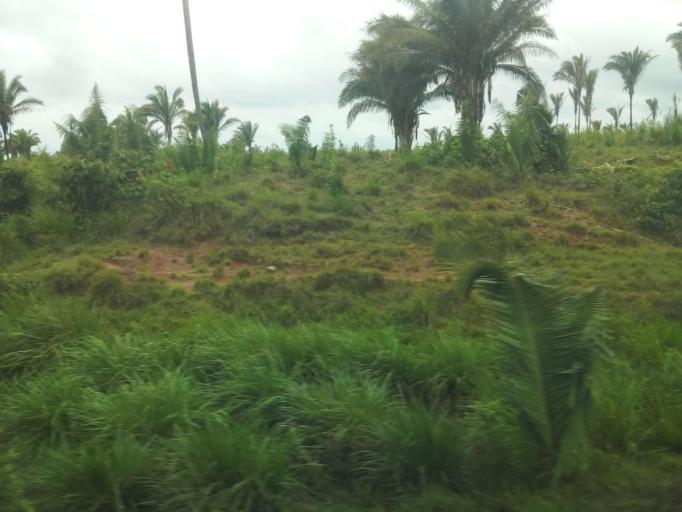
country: BR
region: Maranhao
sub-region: Moncao
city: Moncao
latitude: -3.5848
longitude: -45.0926
